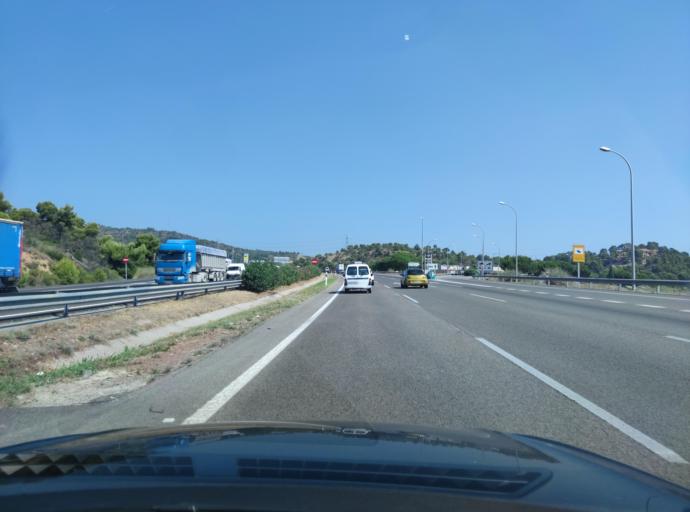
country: ES
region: Valencia
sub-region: Provincia de Valencia
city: Pucol
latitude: 39.6474
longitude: -0.3004
